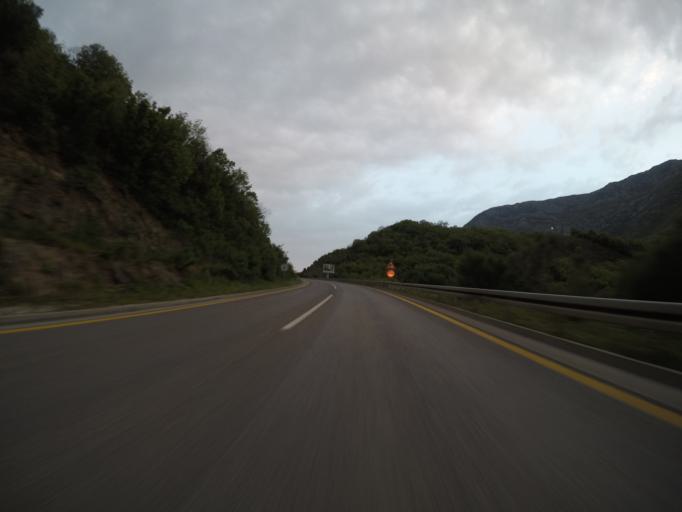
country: ME
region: Bar
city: Sutomore
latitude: 42.1575
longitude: 19.0256
